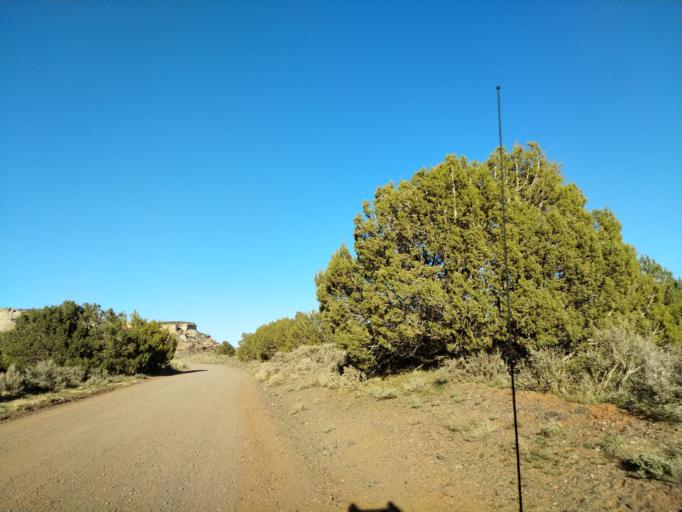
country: US
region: Colorado
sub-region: Mesa County
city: Loma
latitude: 38.9515
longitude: -109.0574
